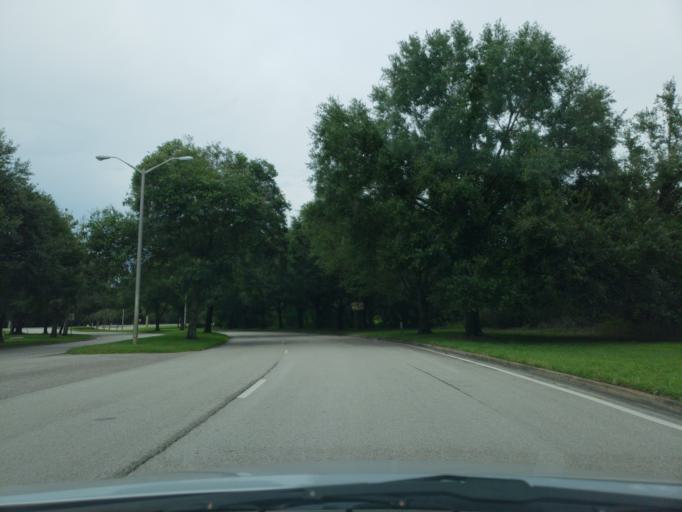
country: US
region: Florida
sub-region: Hillsborough County
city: Temple Terrace
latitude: 28.0674
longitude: -82.3700
